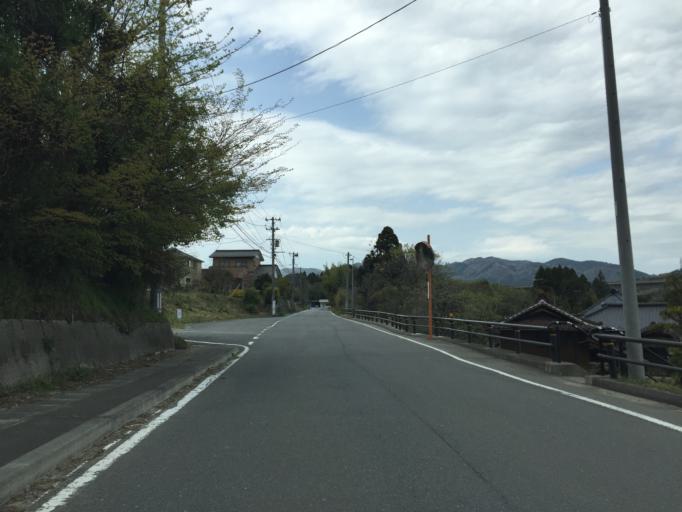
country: JP
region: Fukushima
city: Iwaki
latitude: 37.1141
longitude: 140.9044
